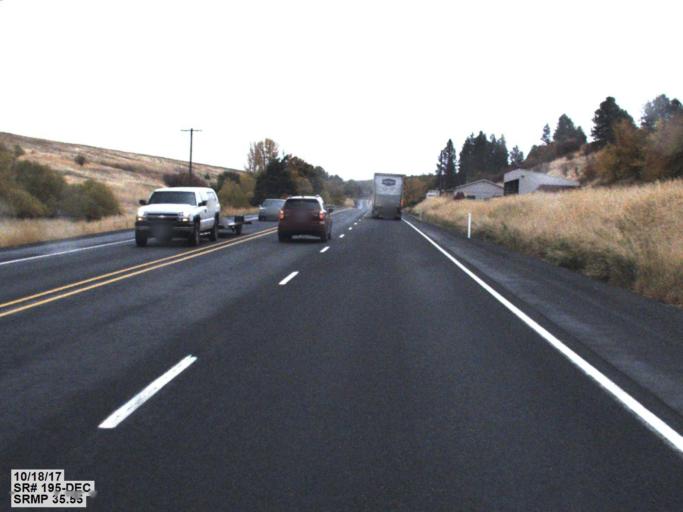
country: US
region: Washington
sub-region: Whitman County
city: Colfax
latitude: 46.8557
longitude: -117.3474
